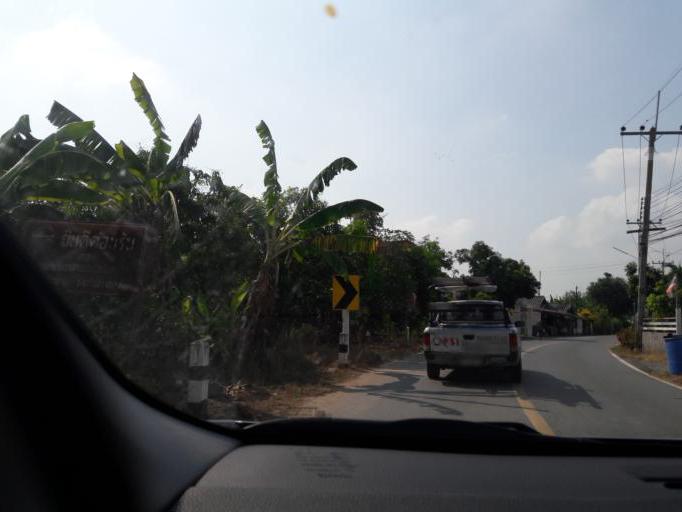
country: TH
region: Ang Thong
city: Ang Thong
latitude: 14.5603
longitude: 100.4291
